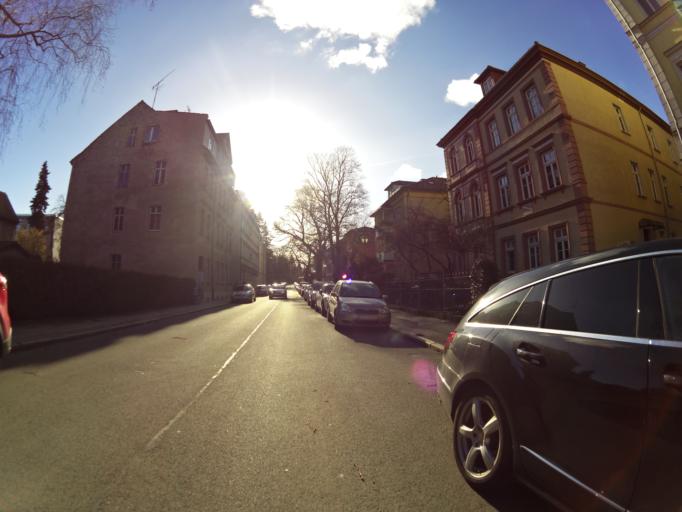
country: DE
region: Thuringia
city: Weimar
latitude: 50.9741
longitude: 11.3283
